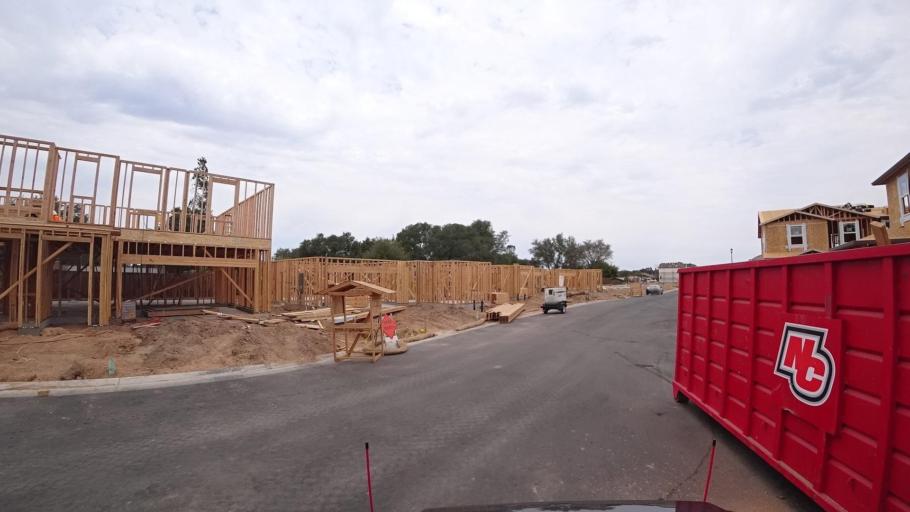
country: US
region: California
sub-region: Placer County
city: Rocklin
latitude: 38.7853
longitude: -121.2187
